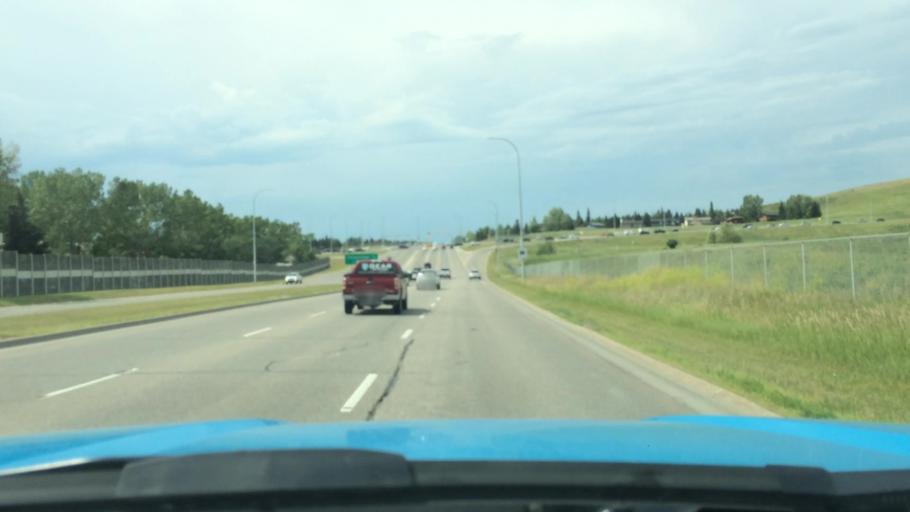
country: CA
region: Alberta
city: Calgary
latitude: 51.1074
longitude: -114.1350
